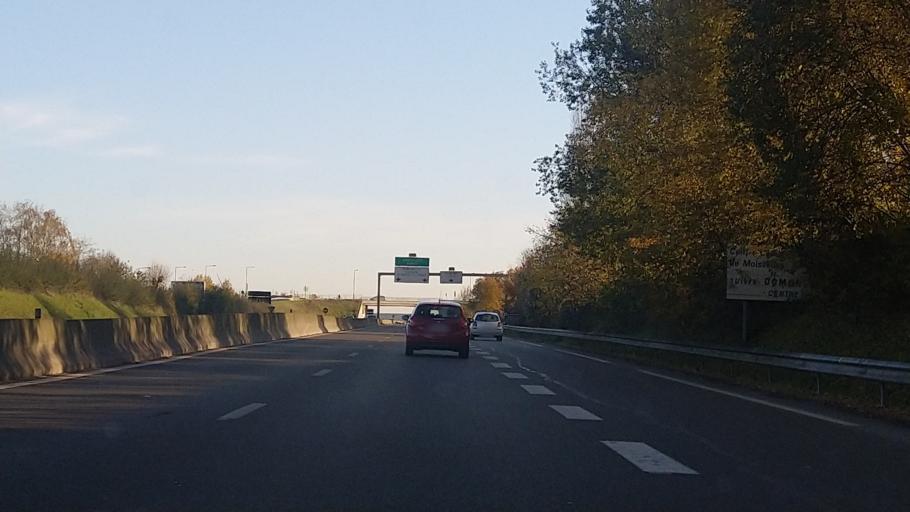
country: FR
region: Ile-de-France
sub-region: Departement du Val-d'Oise
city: Moisselles
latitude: 49.0461
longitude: 2.3343
